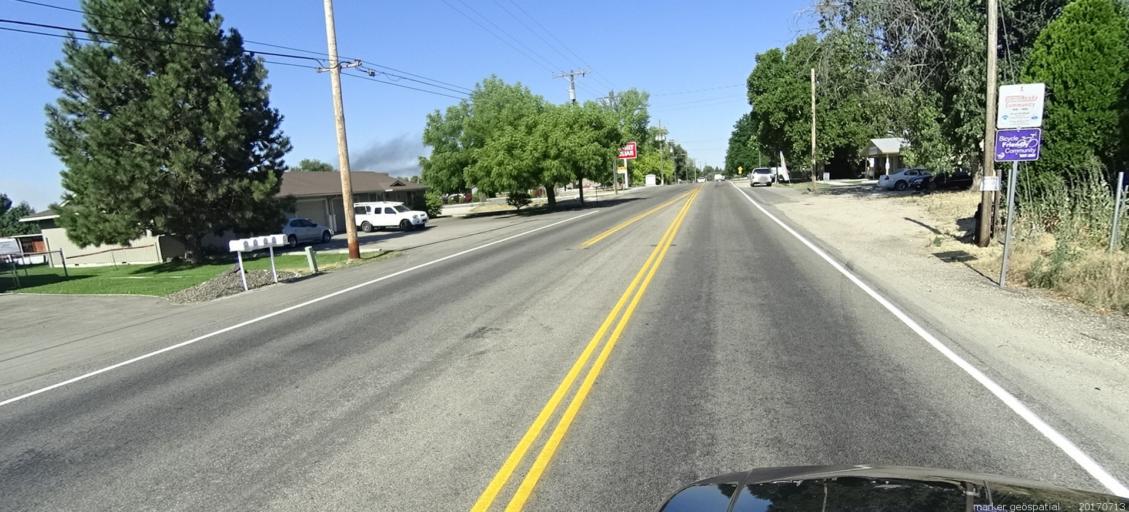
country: US
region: Idaho
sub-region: Ada County
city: Kuna
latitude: 43.4885
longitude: -116.4092
